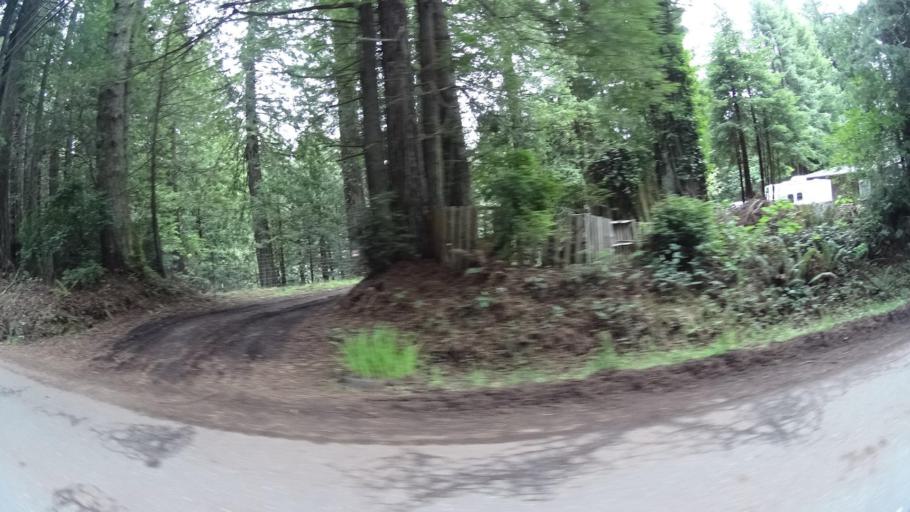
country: US
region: California
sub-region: Humboldt County
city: Bayside
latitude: 40.7938
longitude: -124.0562
